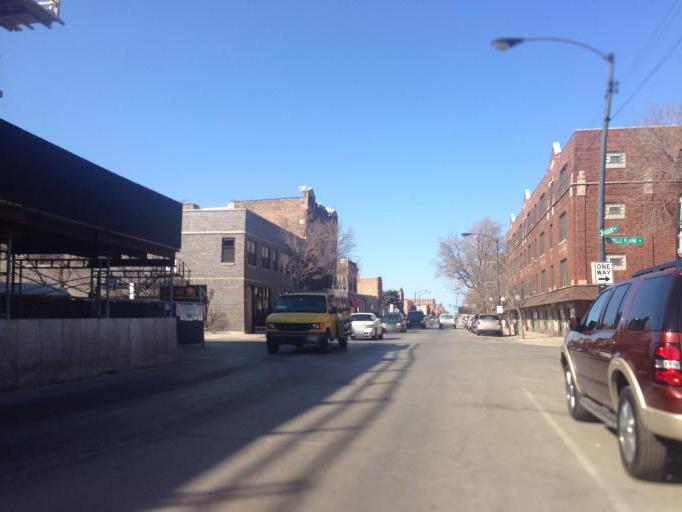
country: US
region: Illinois
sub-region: Cook County
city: Lincolnwood
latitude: 41.9555
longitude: -87.7080
